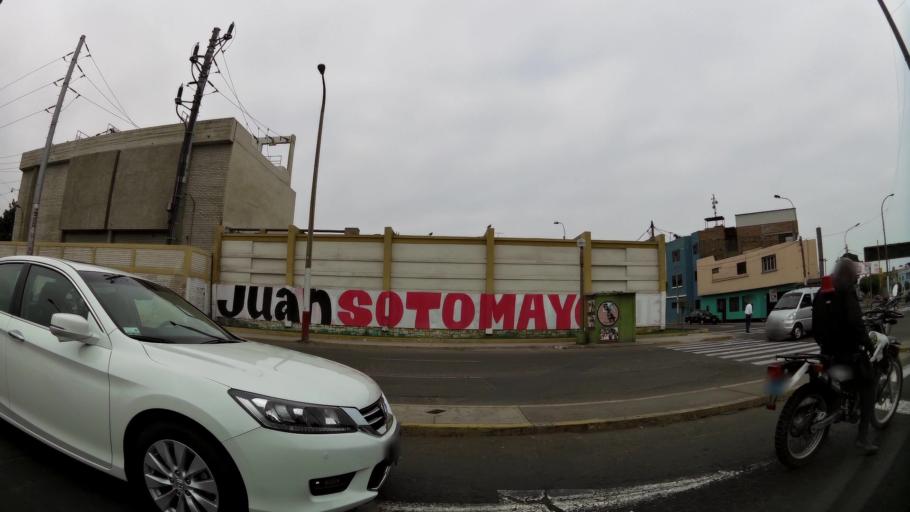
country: PE
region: Callao
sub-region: Callao
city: Callao
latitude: -12.0555
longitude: -77.1333
